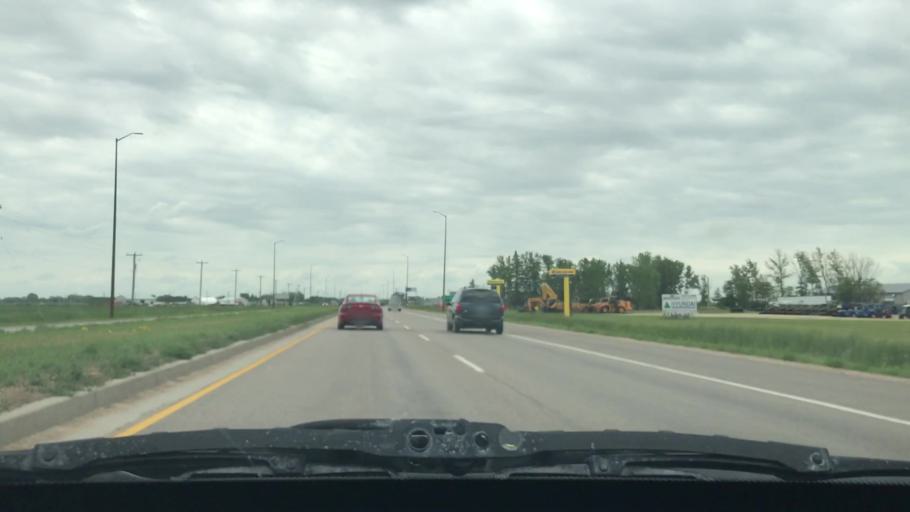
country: CA
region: Manitoba
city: Winnipeg
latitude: 49.8516
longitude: -97.0034
